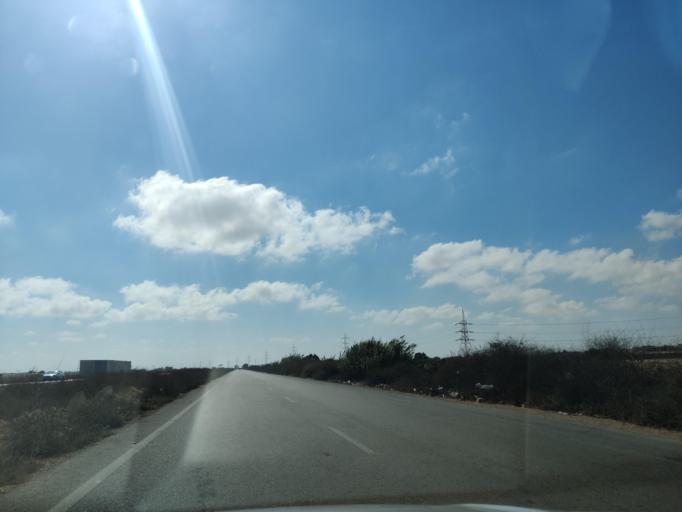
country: EG
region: Muhafazat Matruh
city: Al `Alamayn
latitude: 31.0567
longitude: 28.2516
